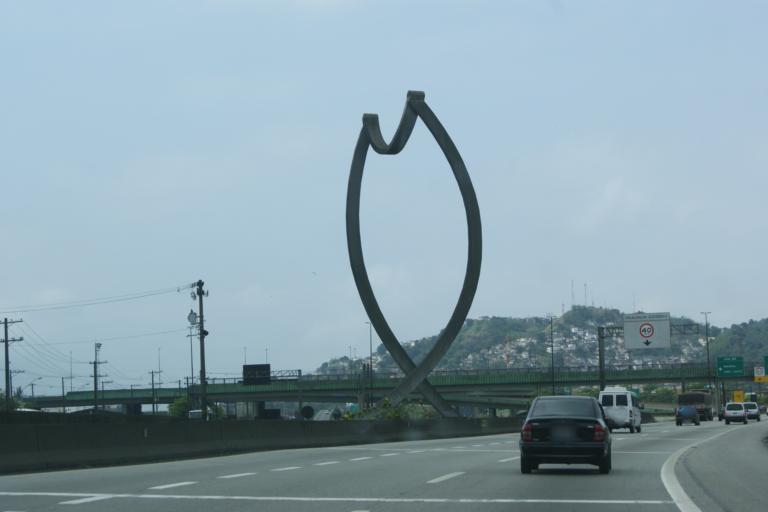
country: BR
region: Sao Paulo
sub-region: Sao Vicente
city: Sao Vicente
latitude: -23.9285
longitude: -46.3674
